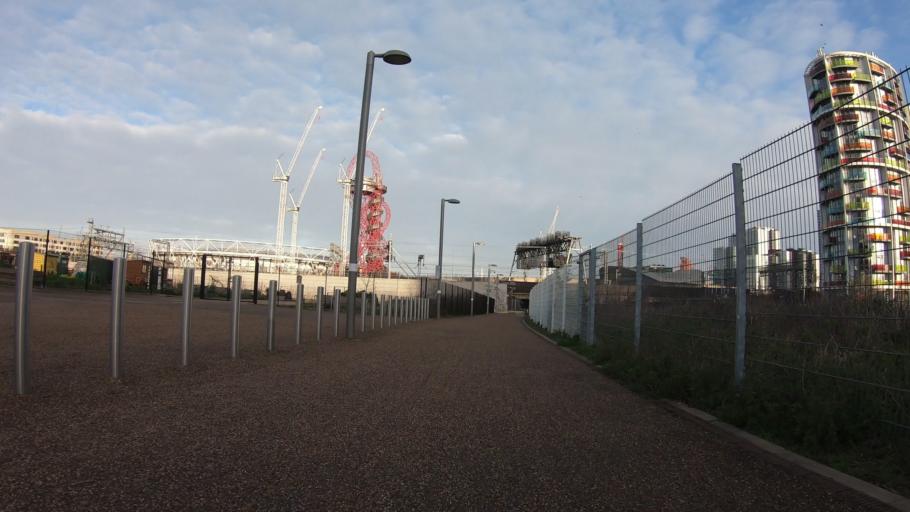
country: GB
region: England
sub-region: Greater London
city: Poplar
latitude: 51.5319
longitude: -0.0077
